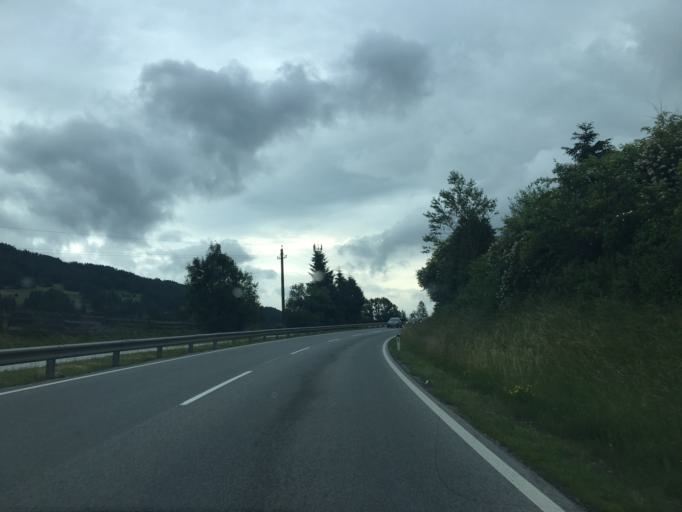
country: AT
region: Tyrol
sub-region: Politischer Bezirk Innsbruck Land
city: Mieders
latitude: 47.1693
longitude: 11.3773
